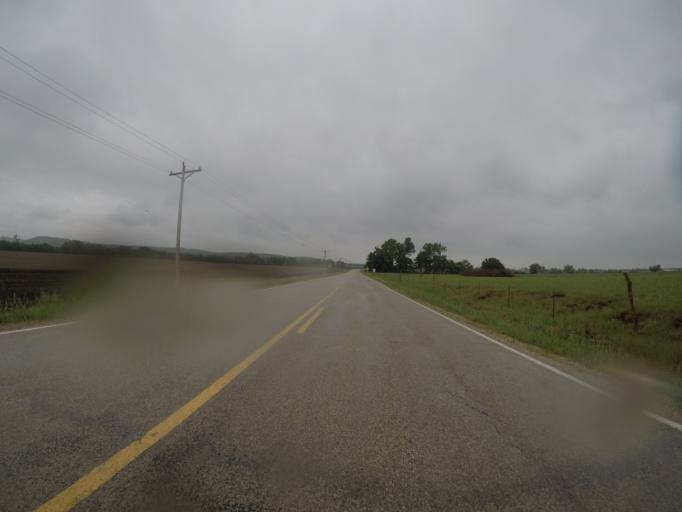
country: US
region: Kansas
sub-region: Pottawatomie County
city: Wamego
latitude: 39.3809
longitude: -96.2072
